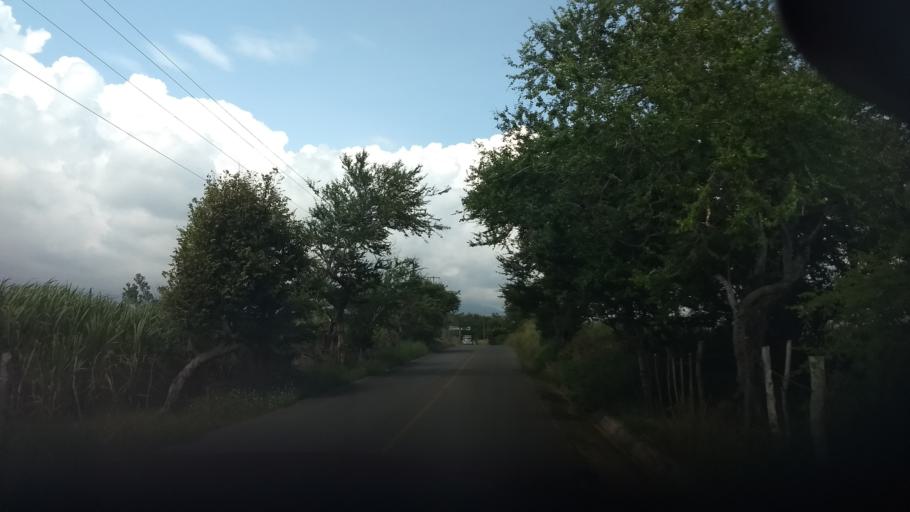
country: MX
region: Jalisco
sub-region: Tonila
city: San Marcos
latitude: 19.4312
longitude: -103.4928
